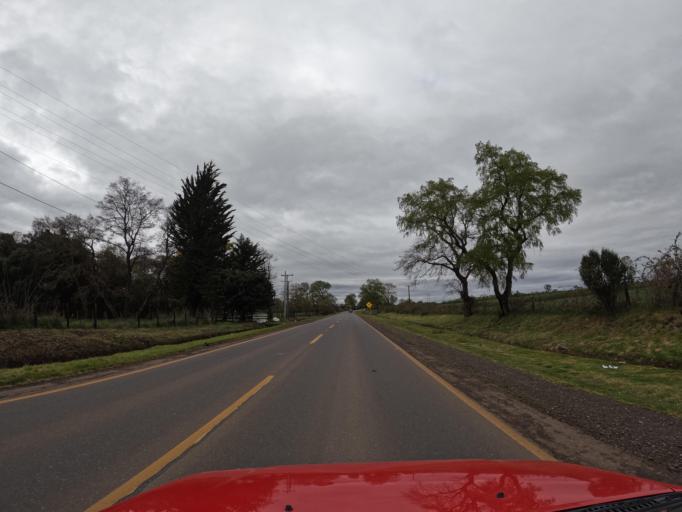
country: CL
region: Araucania
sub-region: Provincia de Malleco
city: Victoria
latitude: -38.2537
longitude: -72.2864
